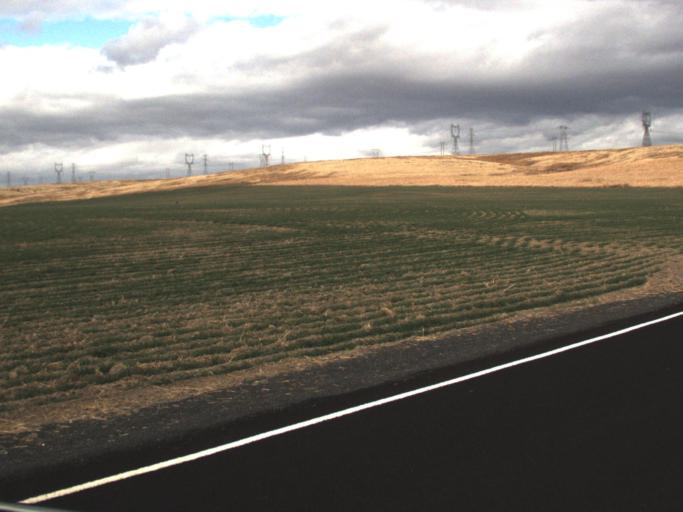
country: US
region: Washington
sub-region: Okanogan County
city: Coulee Dam
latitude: 47.8372
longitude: -118.7181
